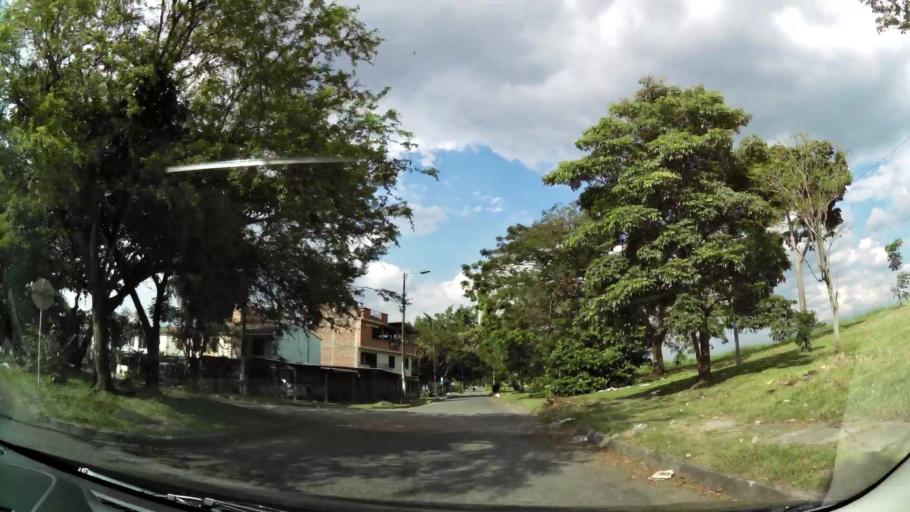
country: CO
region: Valle del Cauca
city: Cali
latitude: 3.3982
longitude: -76.5017
